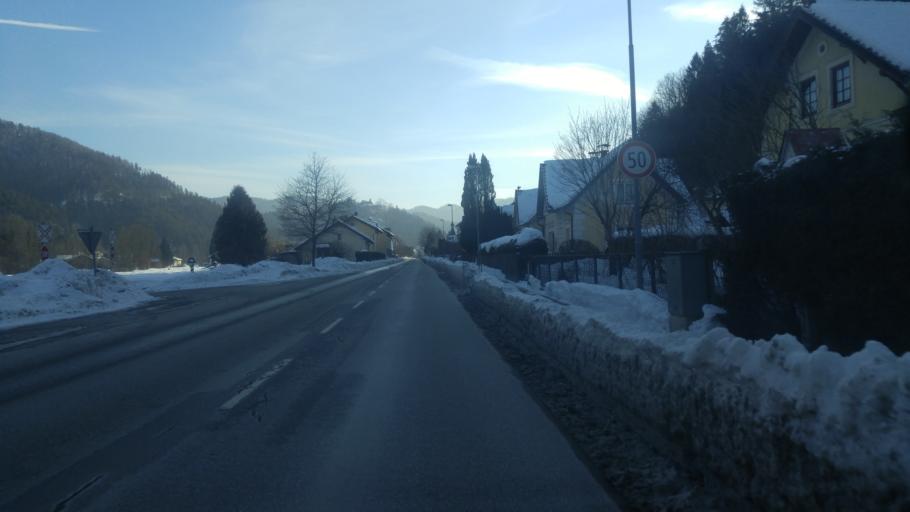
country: AT
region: Lower Austria
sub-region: Politischer Bezirk Lilienfeld
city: Hohenberg
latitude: 47.9156
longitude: 15.6168
